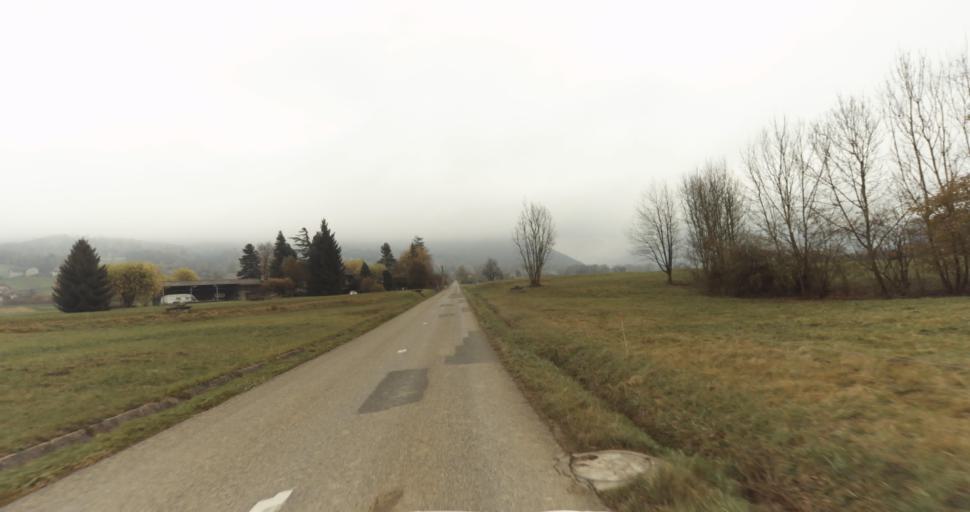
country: FR
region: Rhone-Alpes
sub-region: Departement de la Haute-Savoie
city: Gruffy
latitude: 45.7932
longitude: 6.0487
